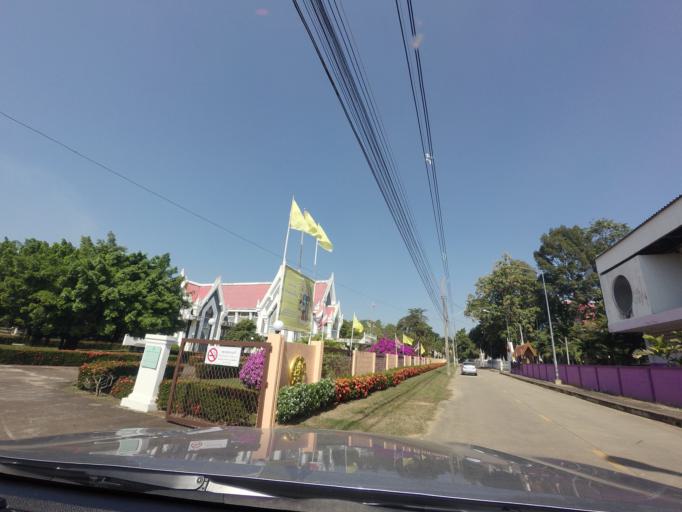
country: TH
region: Sukhothai
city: Sawankhalok
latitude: 17.3194
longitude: 99.8267
